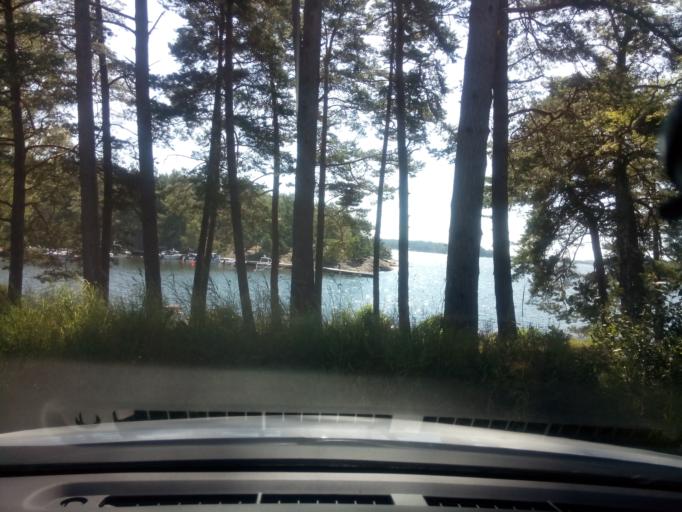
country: SE
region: Soedermanland
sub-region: Oxelosunds Kommun
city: Oxelosund
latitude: 58.7248
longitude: 17.2458
